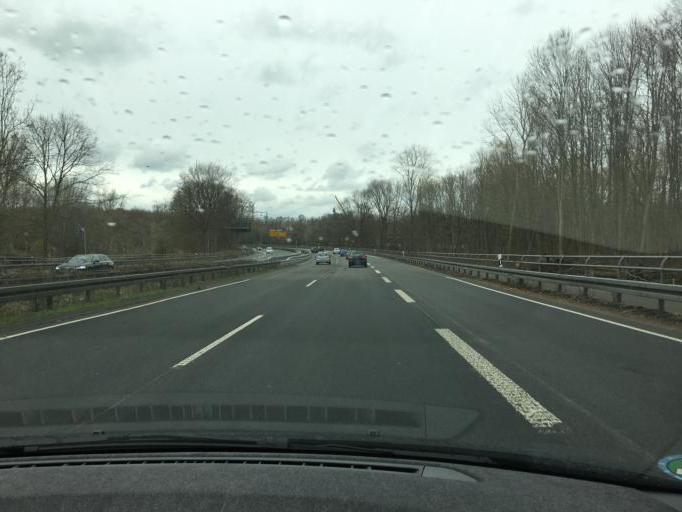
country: DE
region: North Rhine-Westphalia
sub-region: Regierungsbezirk Arnsberg
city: Dortmund
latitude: 51.4777
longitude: 7.4808
